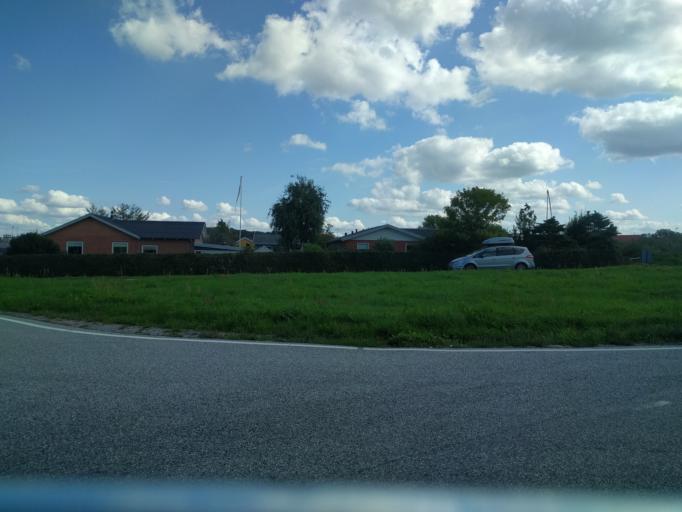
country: DK
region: Central Jutland
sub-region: Skive Kommune
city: Skive
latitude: 56.5925
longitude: 9.0279
